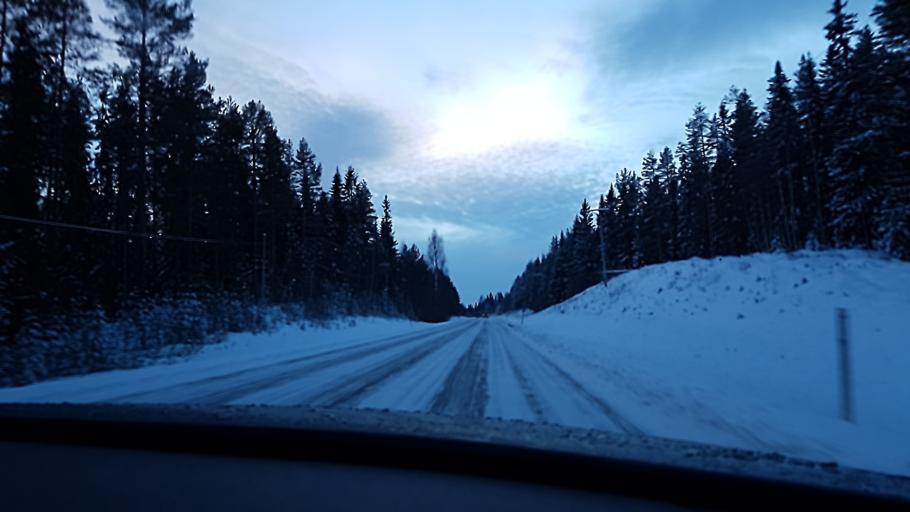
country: SE
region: Jaemtland
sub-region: Harjedalens Kommun
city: Sveg
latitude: 62.0818
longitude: 14.9474
